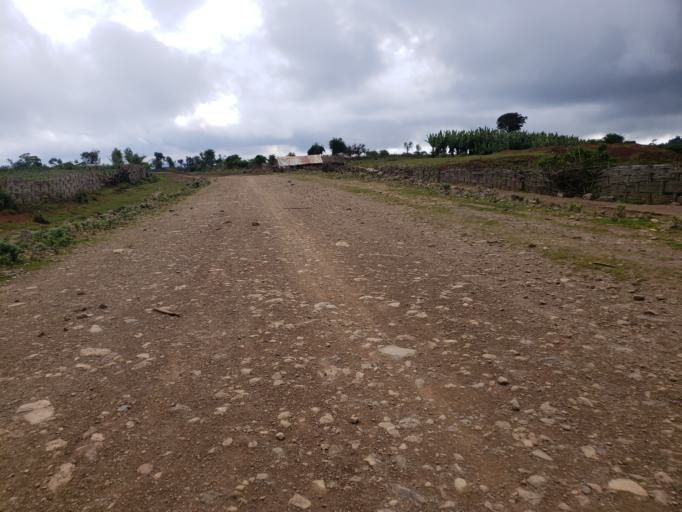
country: ET
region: Oromiya
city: Dodola
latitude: 6.7020
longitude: 39.3727
